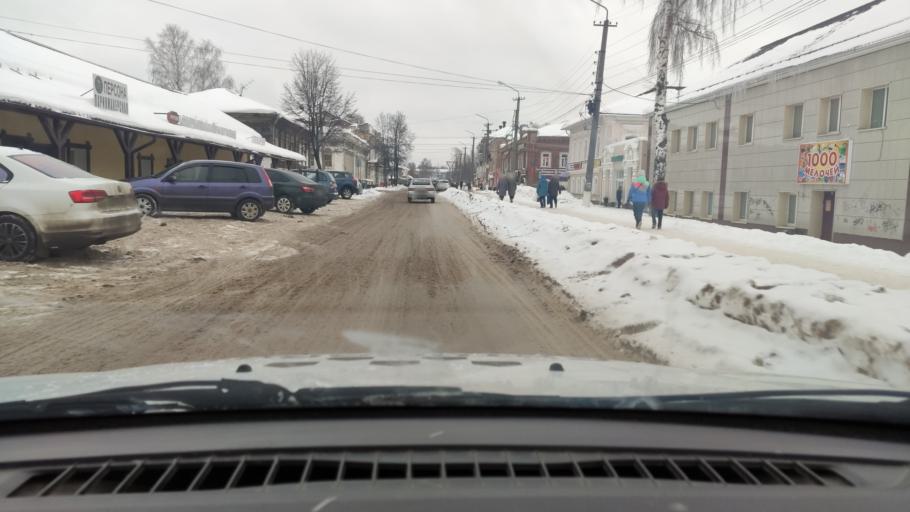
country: RU
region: Perm
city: Kungur
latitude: 57.4384
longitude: 56.9354
